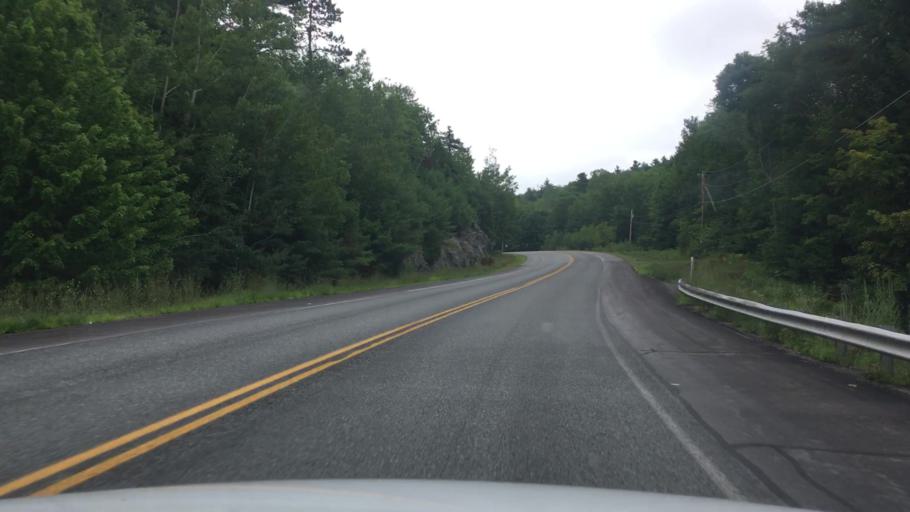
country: US
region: Maine
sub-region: Penobscot County
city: Bradley
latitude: 44.8193
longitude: -68.5035
